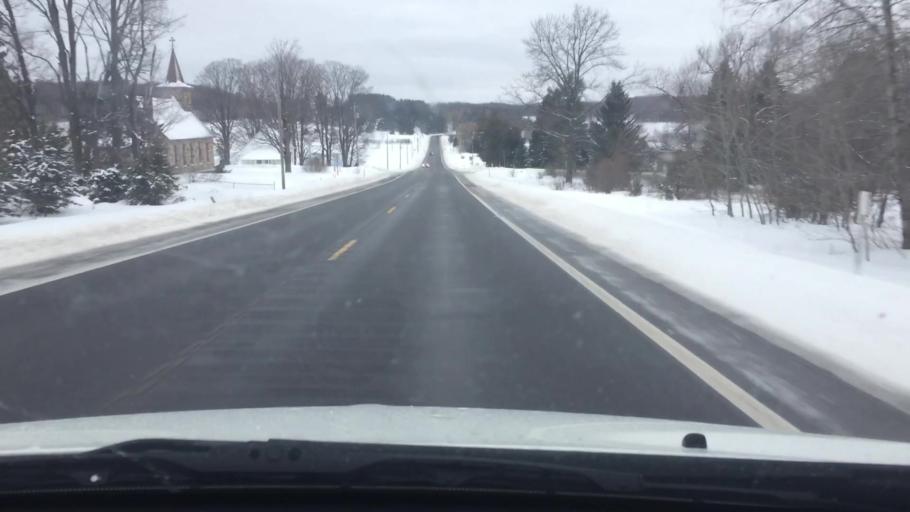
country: US
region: Michigan
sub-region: Charlevoix County
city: East Jordan
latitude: 45.1035
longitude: -85.0384
